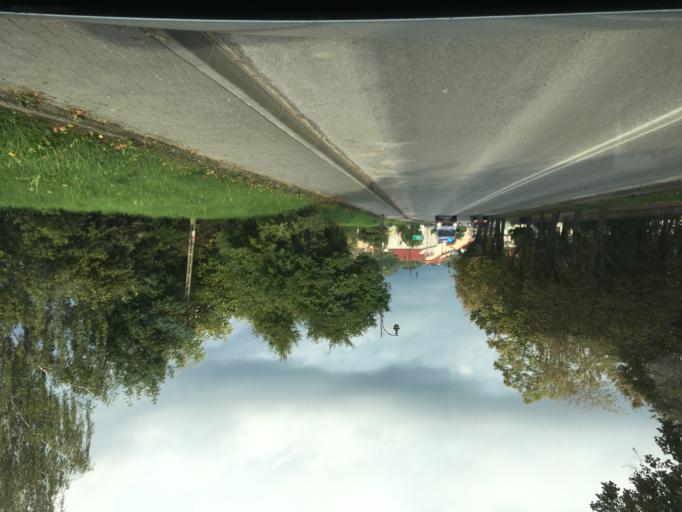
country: PL
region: Swietokrzyskie
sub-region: Powiat pinczowski
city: Pinczow
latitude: 50.5166
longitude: 20.5229
